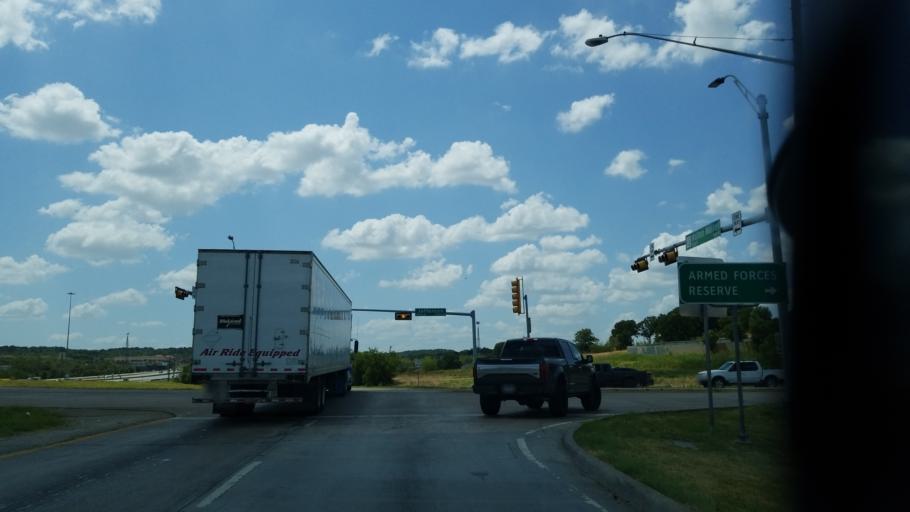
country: US
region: Texas
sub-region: Dallas County
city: Cockrell Hill
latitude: 32.7483
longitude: -96.9206
